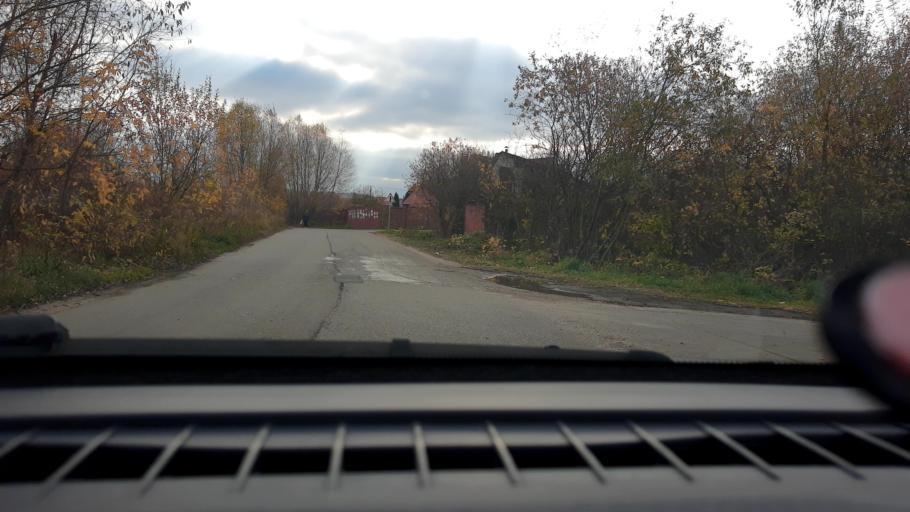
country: RU
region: Nizjnij Novgorod
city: Afonino
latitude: 56.2011
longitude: 44.0958
